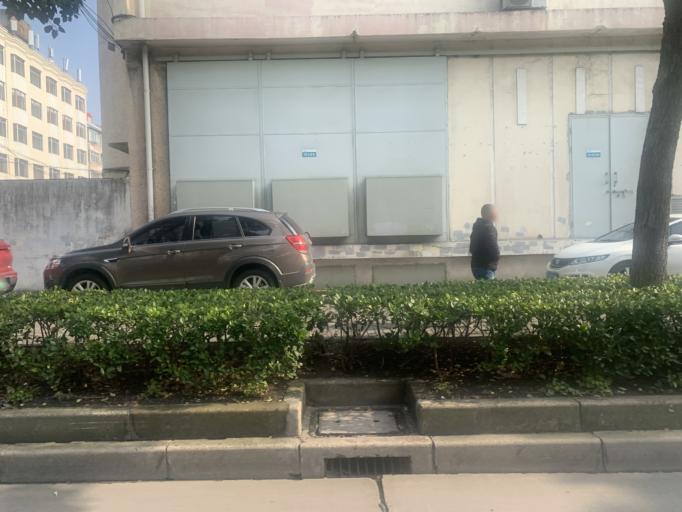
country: CN
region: Shanghai Shi
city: Huamu
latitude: 31.1869
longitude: 121.5141
